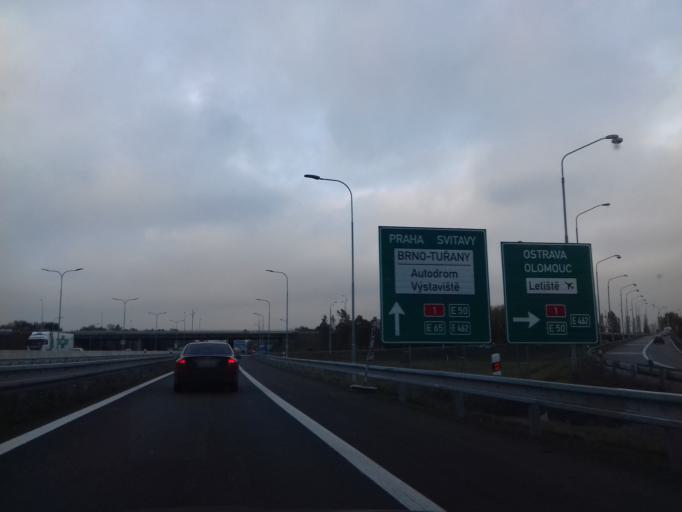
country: CZ
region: South Moravian
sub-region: Mesto Brno
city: Brno
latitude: 49.1572
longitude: 16.6308
